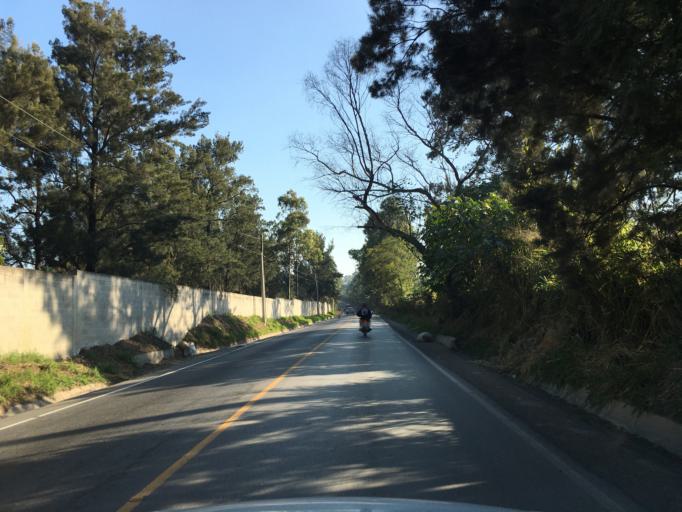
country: GT
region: Guatemala
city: Villa Nueva
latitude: 14.5257
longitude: -90.6168
